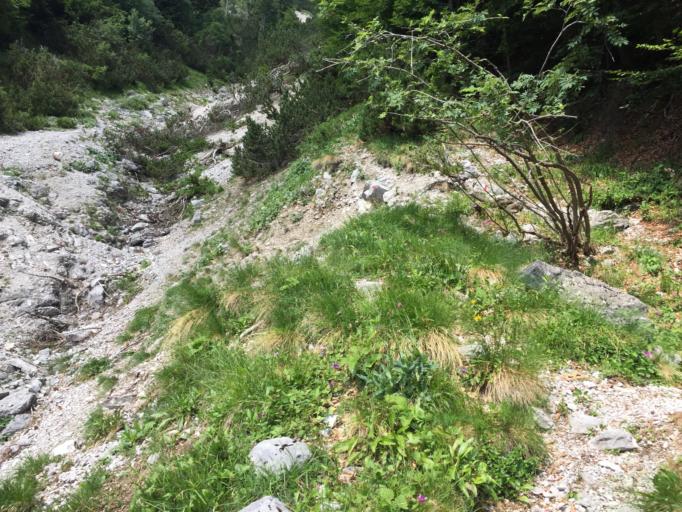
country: IT
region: Friuli Venezia Giulia
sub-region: Provincia di Udine
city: Malborghetto
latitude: 46.4687
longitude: 13.4305
